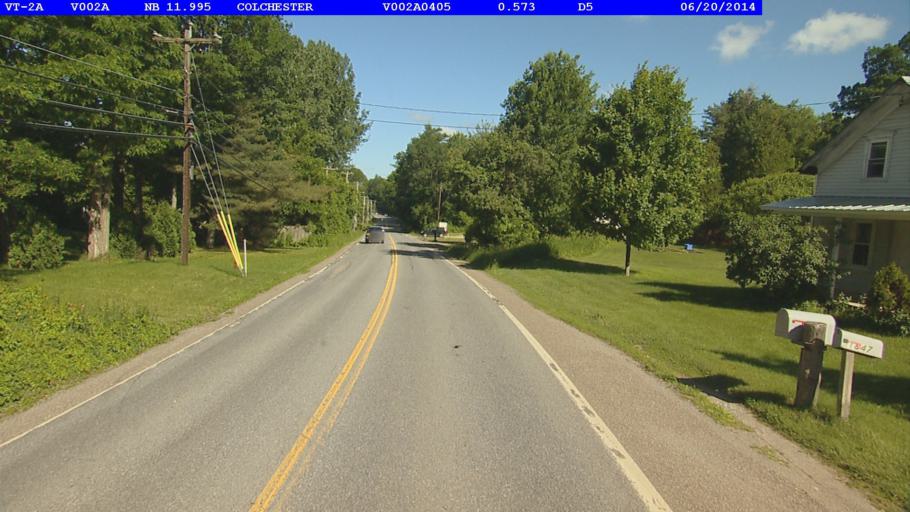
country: US
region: Vermont
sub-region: Chittenden County
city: Colchester
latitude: 44.5354
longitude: -73.1348
